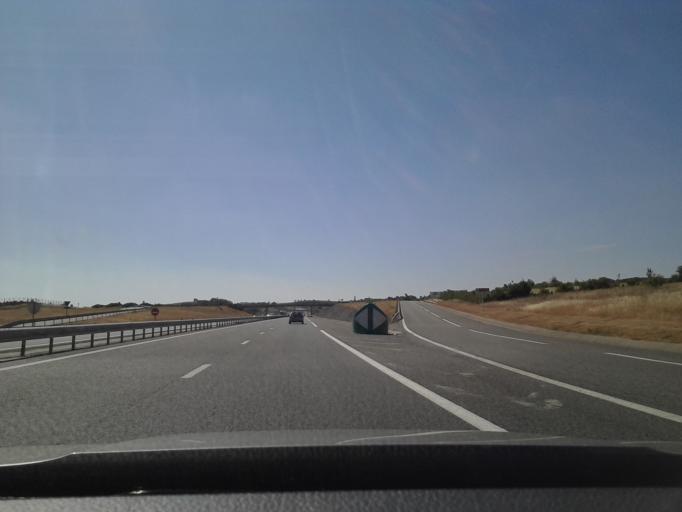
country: FR
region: Midi-Pyrenees
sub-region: Departement de l'Aveyron
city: La Cavalerie
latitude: 44.0145
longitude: 3.1373
